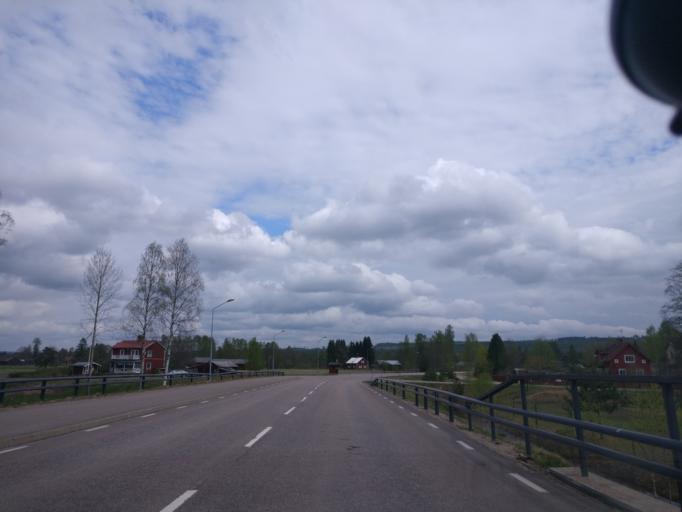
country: SE
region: Vaermland
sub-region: Hagfors Kommun
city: Ekshaerad
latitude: 60.1765
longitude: 13.5055
